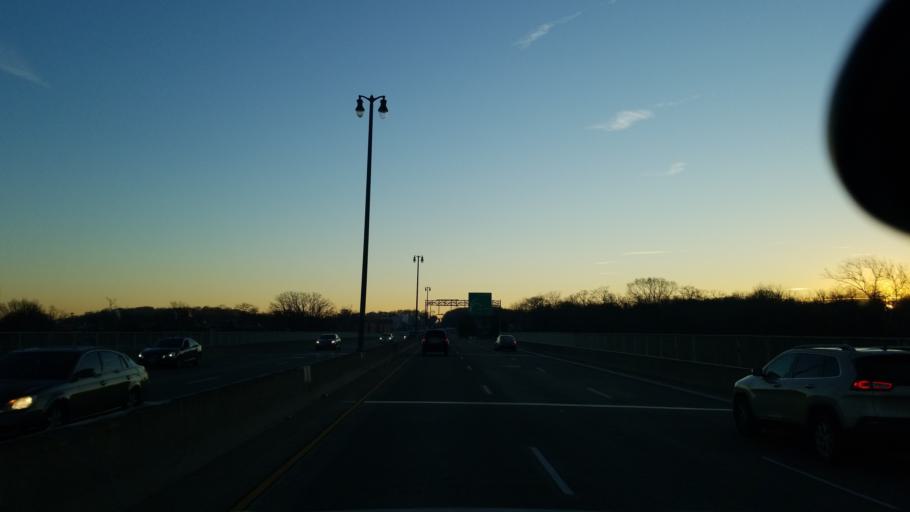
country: US
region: Maryland
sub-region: Prince George's County
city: Colmar Manor
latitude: 38.8898
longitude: -76.9643
